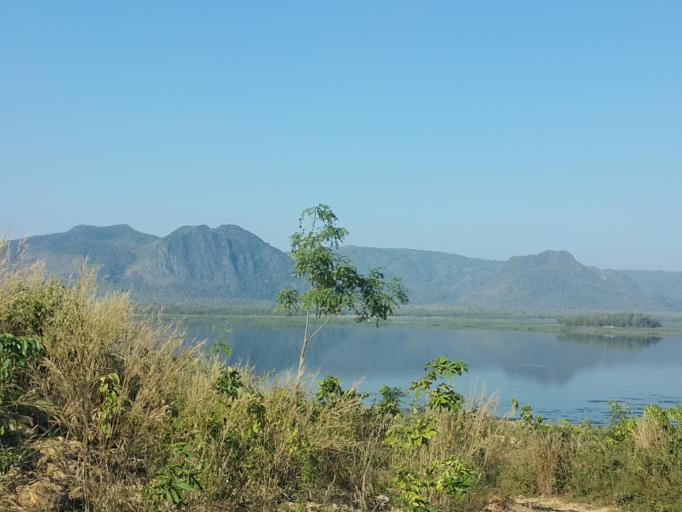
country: TH
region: Sukhothai
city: Thung Saliam
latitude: 17.3099
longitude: 99.4257
